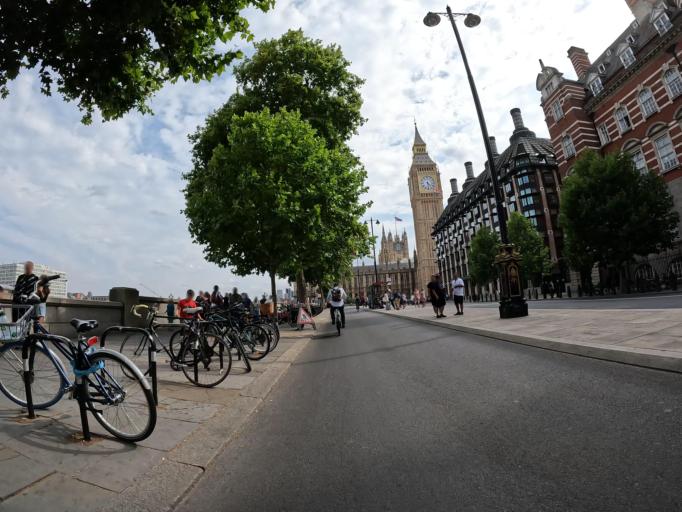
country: GB
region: England
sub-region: Greater London
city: Orpington
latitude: 51.3623
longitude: 0.0541
